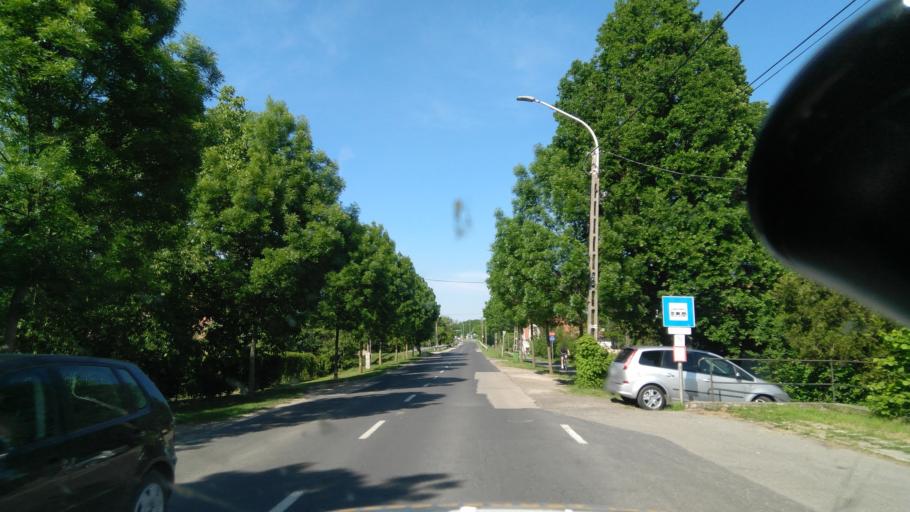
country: HU
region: Bekes
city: Gyula
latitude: 46.6621
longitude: 21.2932
